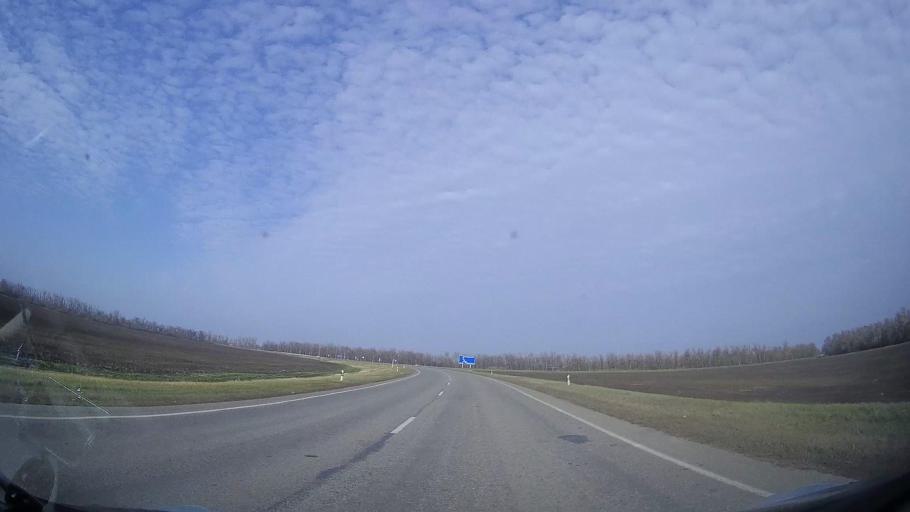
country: RU
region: Rostov
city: Tselina
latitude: 46.5284
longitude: 40.9901
